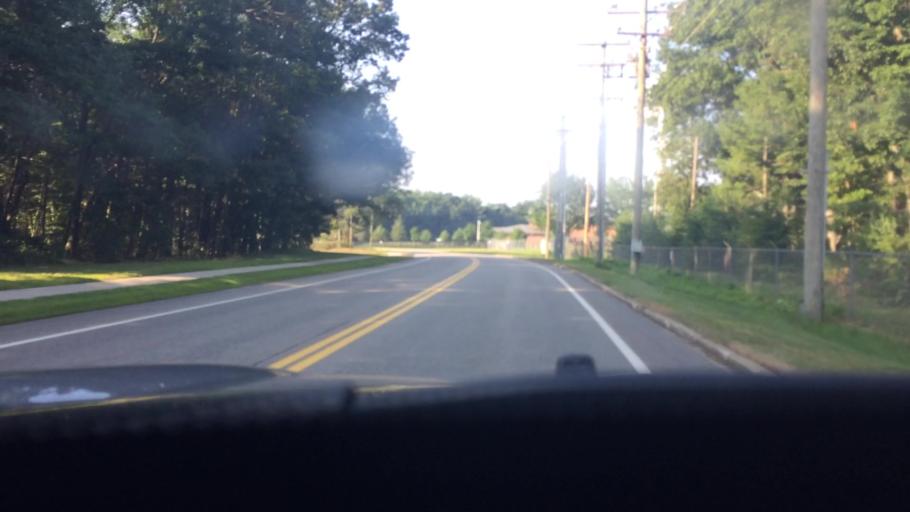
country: US
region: Maine
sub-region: York County
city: South Eliot
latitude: 43.0904
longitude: -70.8133
